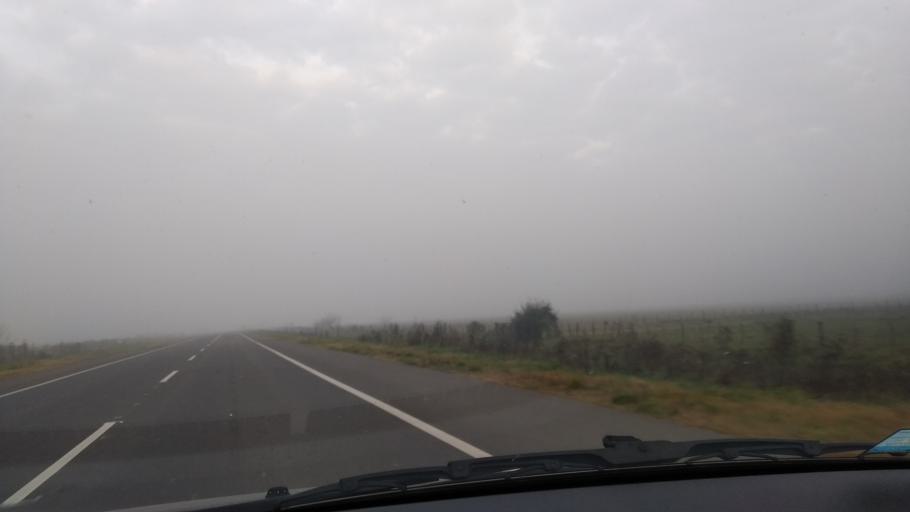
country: AR
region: Buenos Aires
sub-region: Partido de San Vicente
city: San Vicente
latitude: -35.2174
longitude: -58.4288
